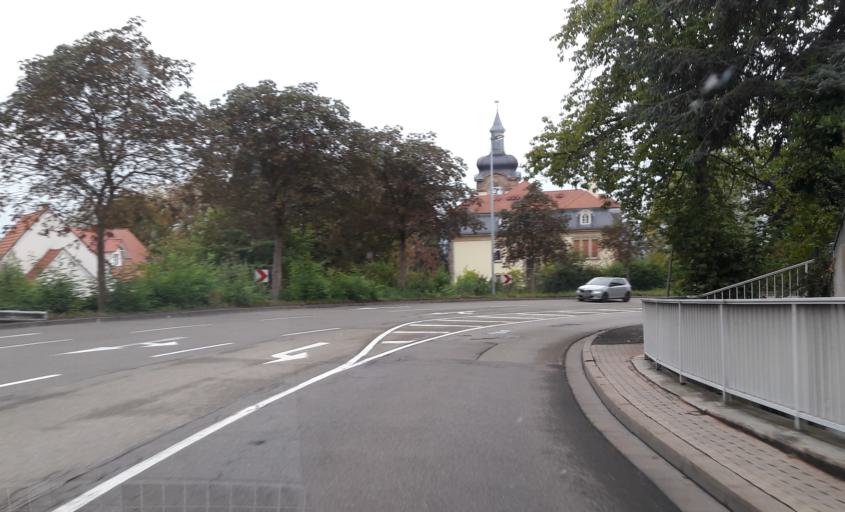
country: DE
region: Rheinland-Pfalz
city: Zweibrucken
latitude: 49.2422
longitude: 7.3754
